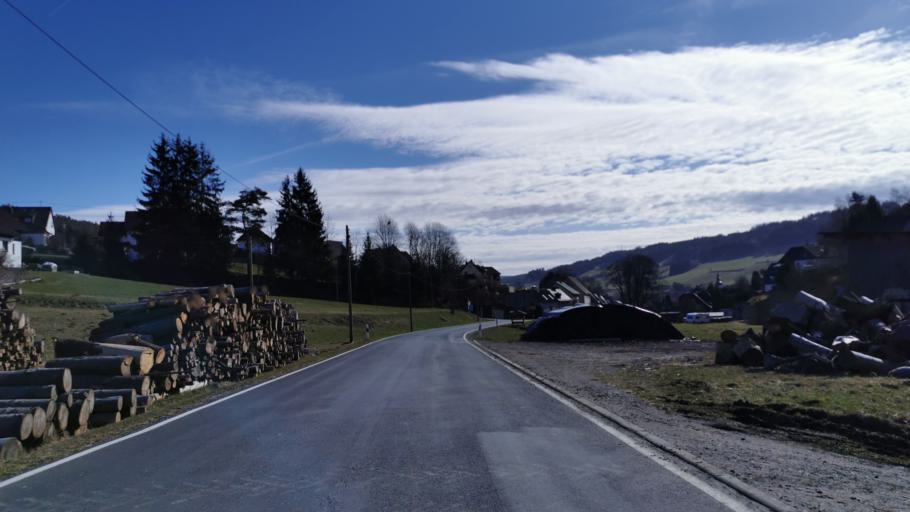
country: DE
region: Thuringia
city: Grafenthal
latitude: 50.4912
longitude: 11.3347
